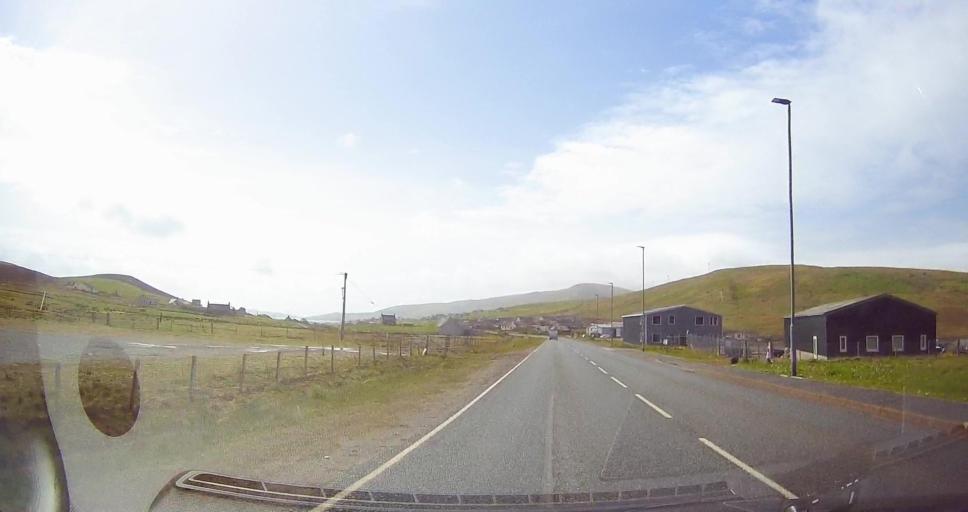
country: GB
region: Scotland
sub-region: Shetland Islands
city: Sandwick
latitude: 60.0584
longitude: -1.2231
